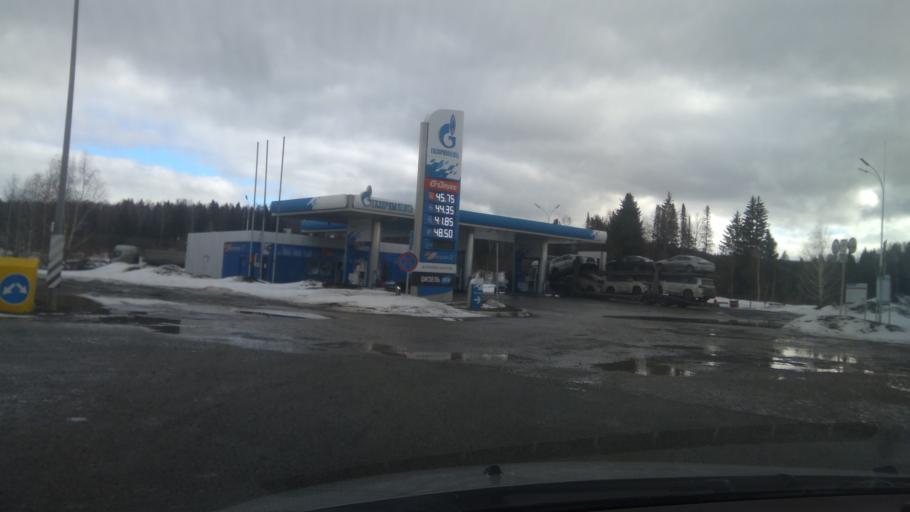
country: RU
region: Sverdlovsk
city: Bisert'
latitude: 56.8298
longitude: 59.0407
